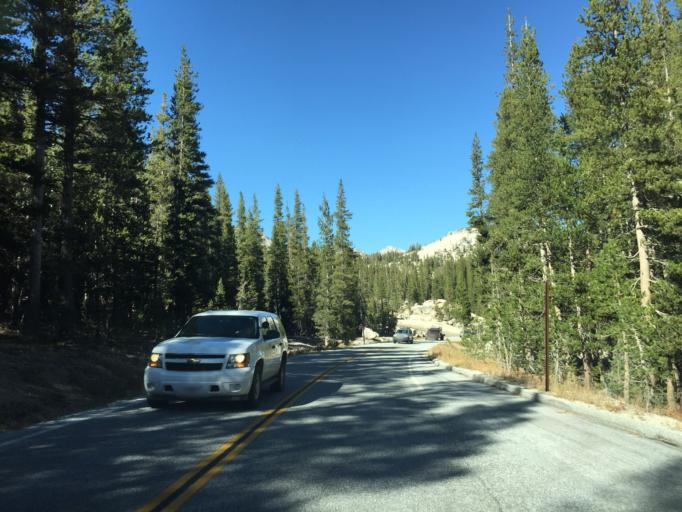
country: US
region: California
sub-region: Mariposa County
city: Yosemite Valley
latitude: 37.8219
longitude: -119.4779
